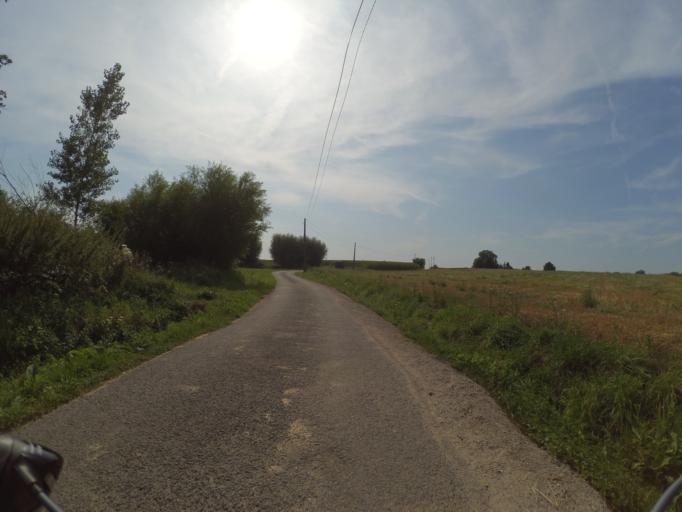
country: BE
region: Wallonia
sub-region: Province du Hainaut
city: Flobecq
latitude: 50.7233
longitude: 3.7170
